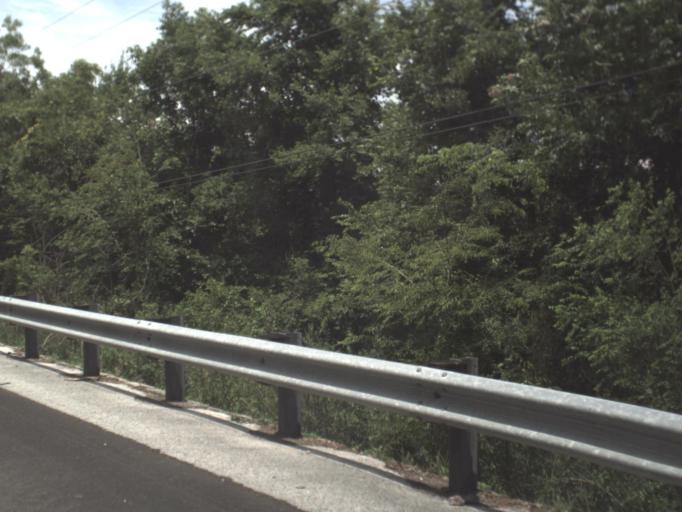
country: US
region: Florida
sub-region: Levy County
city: Williston
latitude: 29.4194
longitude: -82.4553
